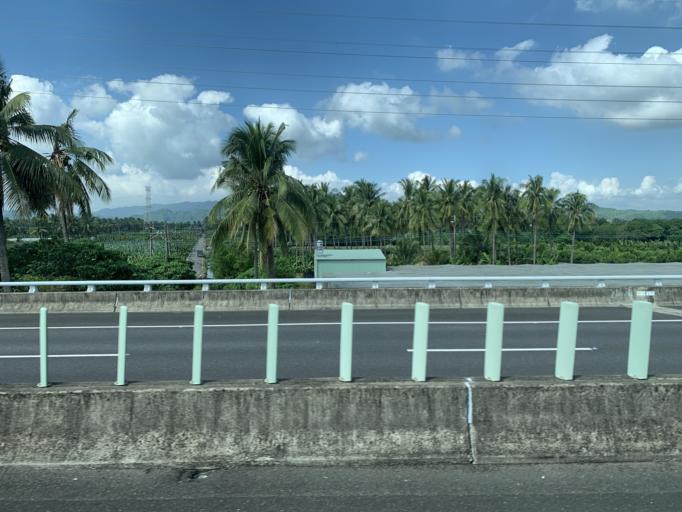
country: TW
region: Taiwan
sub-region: Pingtung
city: Pingtung
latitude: 22.8438
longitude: 120.4960
